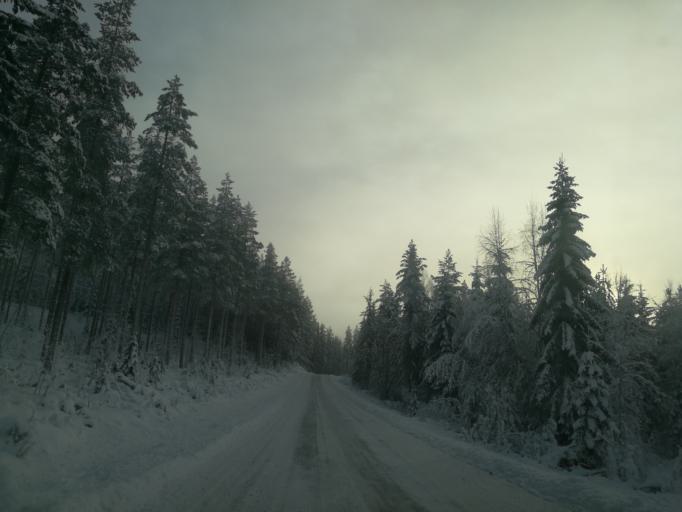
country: SE
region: Vaermland
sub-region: Torsby Kommun
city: Torsby
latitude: 60.6467
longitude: 12.7287
